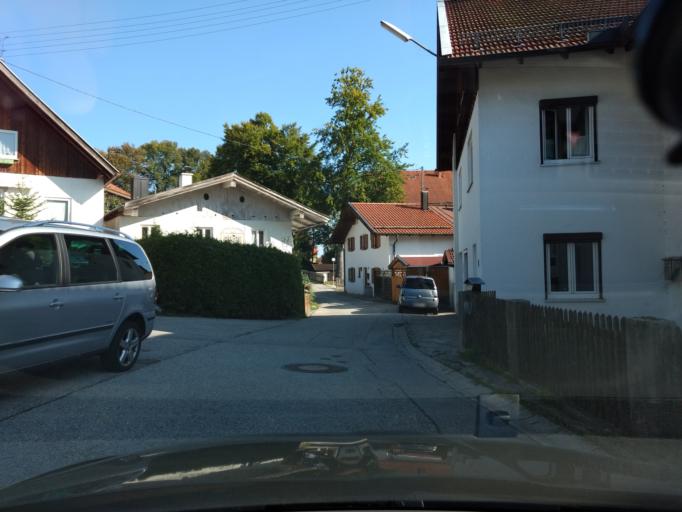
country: DE
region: Bavaria
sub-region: Upper Bavaria
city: Wolfratshausen
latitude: 47.9090
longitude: 11.4154
